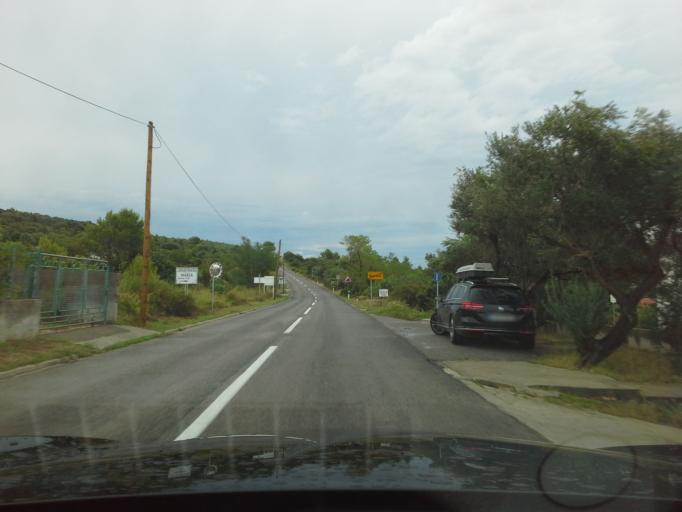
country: HR
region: Primorsko-Goranska
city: Banjol
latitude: 44.7257
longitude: 14.8179
